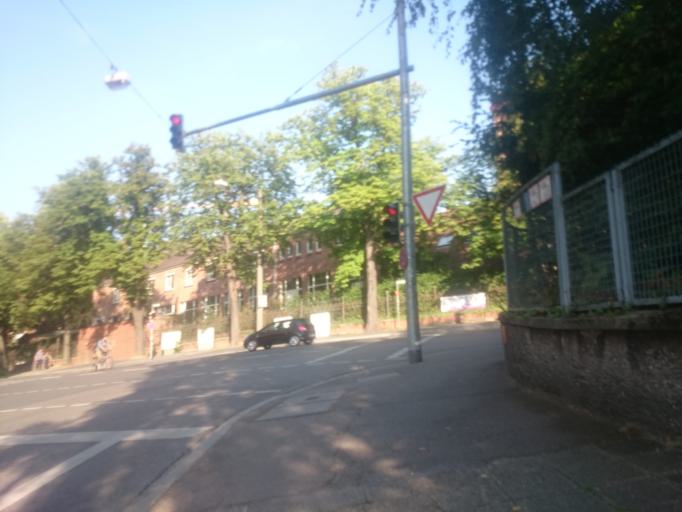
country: DE
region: Bavaria
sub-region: Swabia
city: Augsburg
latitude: 48.3685
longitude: 10.8859
